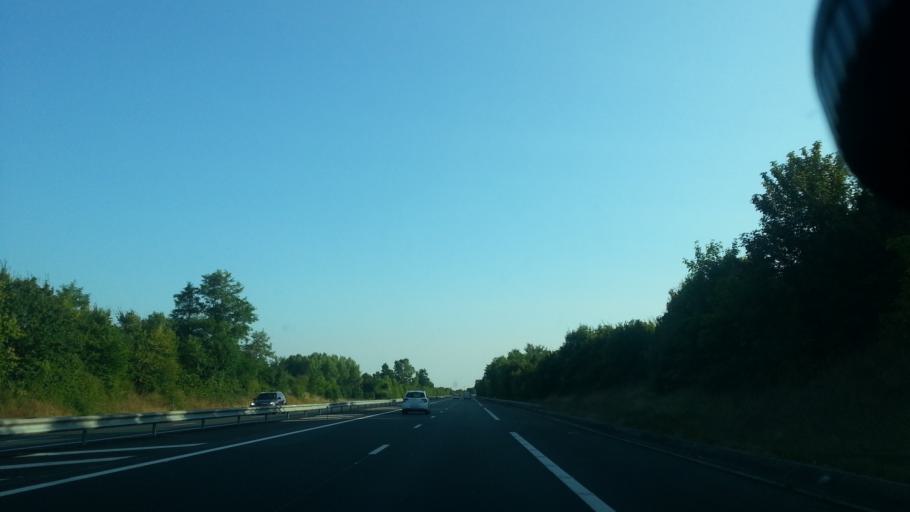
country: FR
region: Poitou-Charentes
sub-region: Departement des Deux-Sevres
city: Beauvoir-sur-Niort
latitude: 46.1253
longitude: -0.5313
